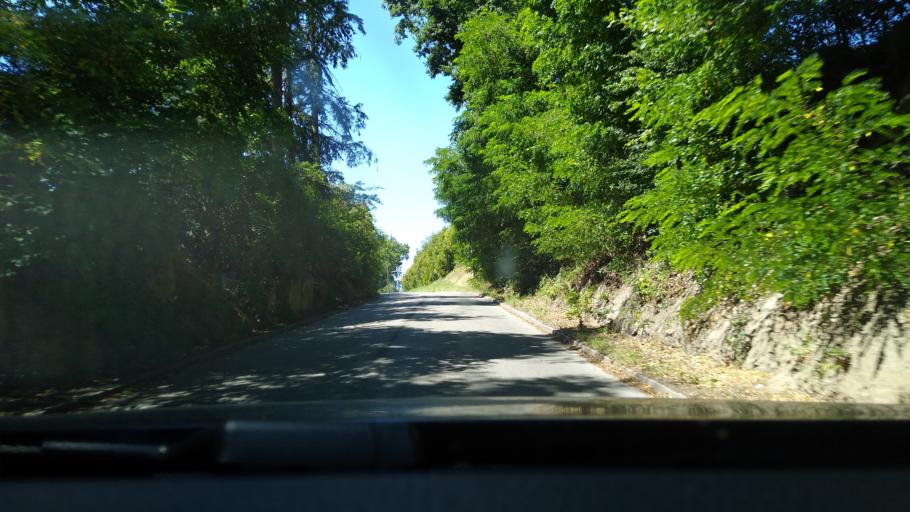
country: DE
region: Bavaria
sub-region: Regierungsbezirk Mittelfranken
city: Cadolzburg
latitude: 49.4605
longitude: 10.8476
